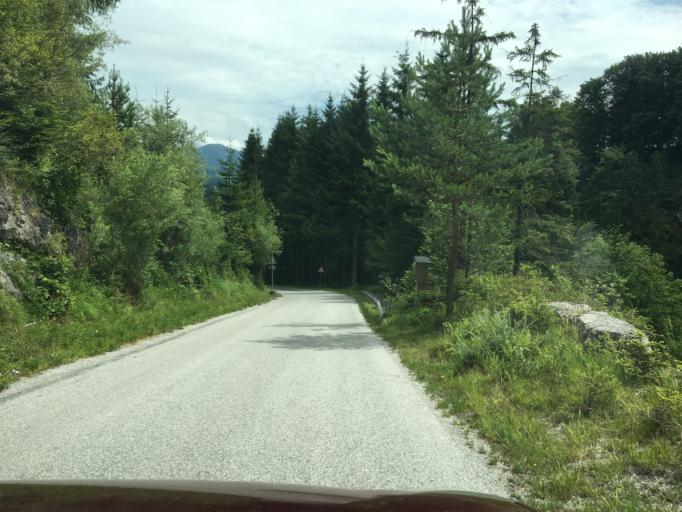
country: AT
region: Salzburg
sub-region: Politischer Bezirk Hallein
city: Scheffau am Tennengebirge
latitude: 47.6004
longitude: 13.2878
